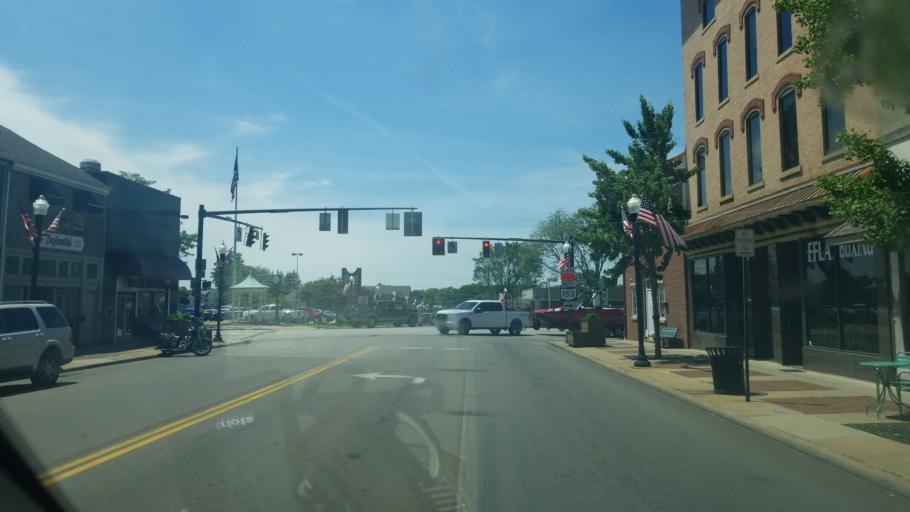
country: US
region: Ohio
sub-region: Stark County
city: Louisville
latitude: 40.8376
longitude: -81.2591
